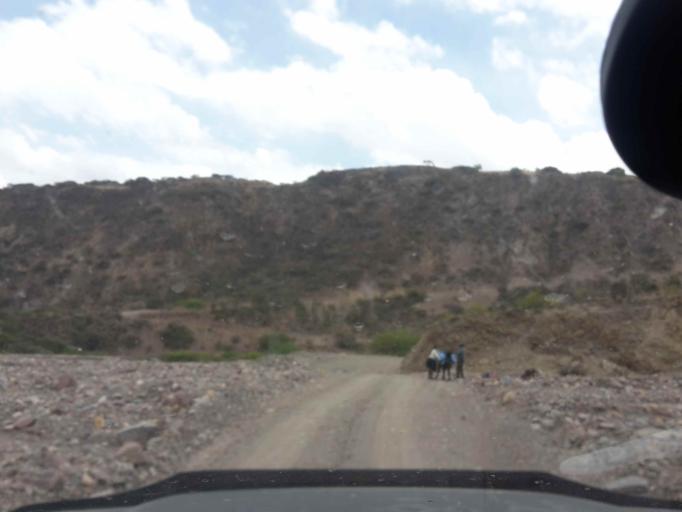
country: BO
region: Cochabamba
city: Sipe Sipe
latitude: -17.5214
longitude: -66.5536
